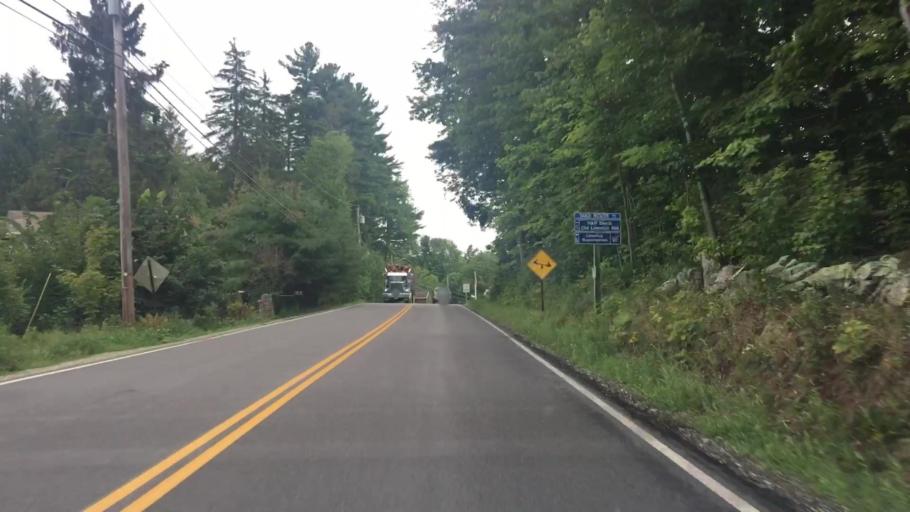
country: US
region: Maine
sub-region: York County
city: Limerick
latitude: 43.6923
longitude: -70.7970
